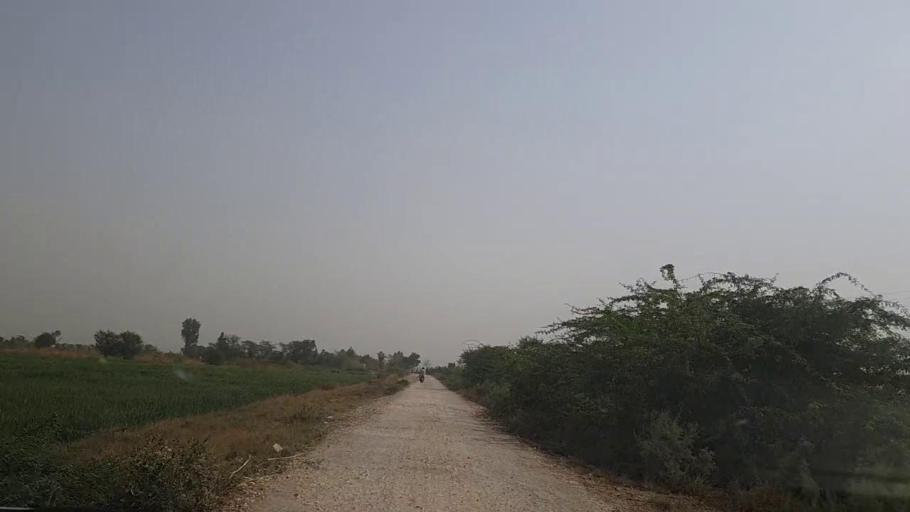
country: PK
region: Sindh
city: Pithoro
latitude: 25.4787
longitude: 69.2214
